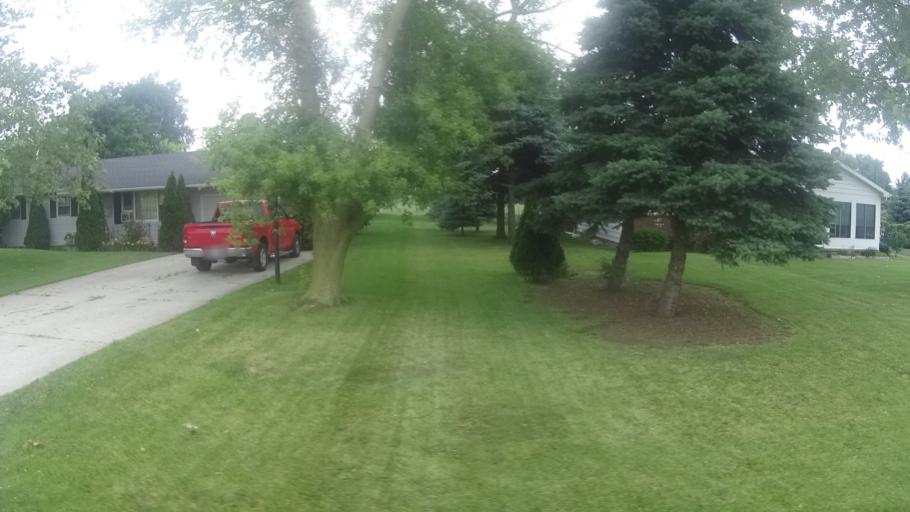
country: US
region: Ohio
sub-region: Huron County
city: Monroeville
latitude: 41.3073
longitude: -82.7066
